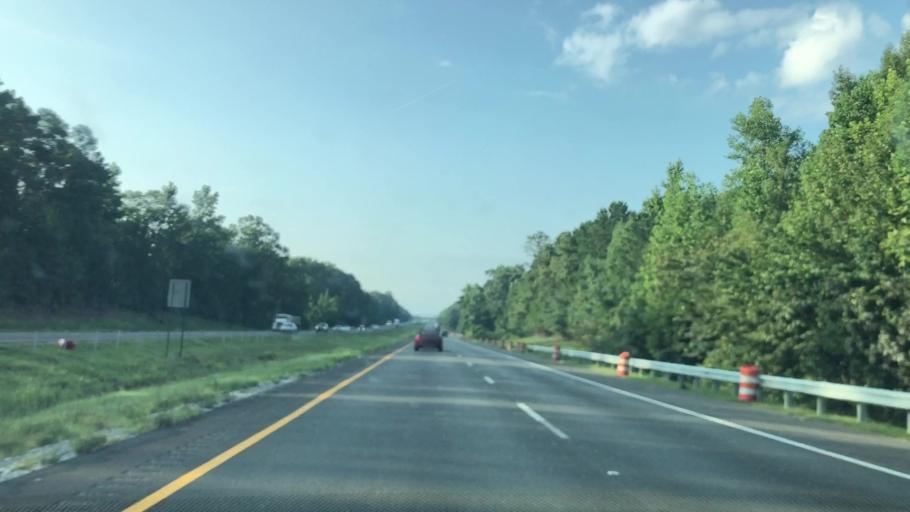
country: US
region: Alabama
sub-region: Chilton County
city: Clanton
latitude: 32.8282
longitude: -86.5900
